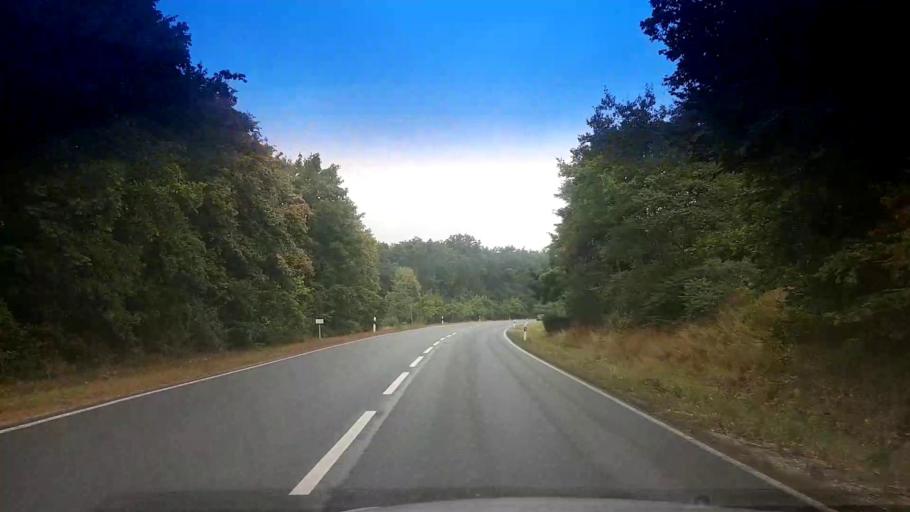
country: DE
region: Bavaria
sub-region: Upper Franconia
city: Forchheim
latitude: 49.7106
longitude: 11.0416
